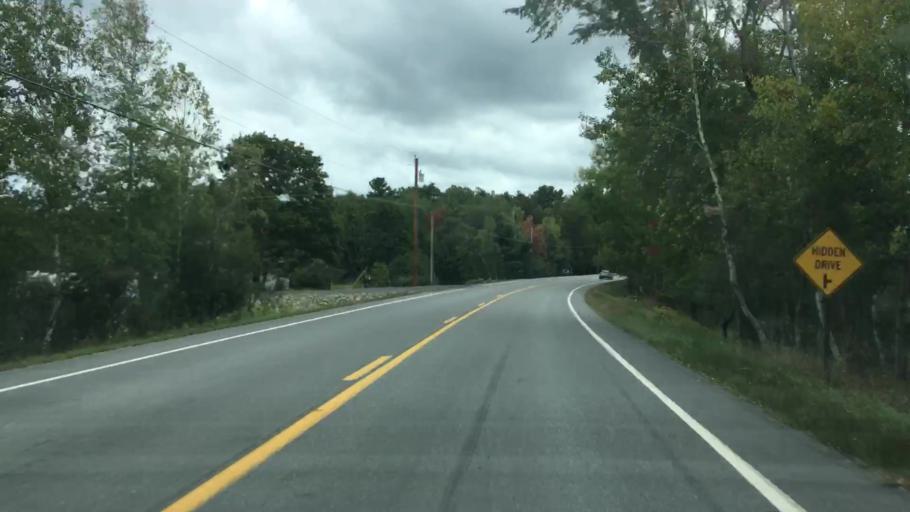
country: US
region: Maine
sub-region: Penobscot County
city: Hermon
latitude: 44.7456
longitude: -68.9669
